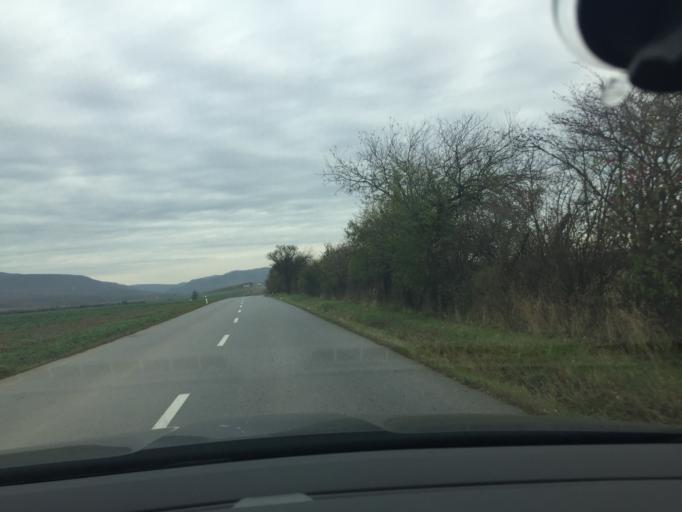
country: SK
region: Presovsky
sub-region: Okres Presov
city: Presov
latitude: 48.9508
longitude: 21.2670
